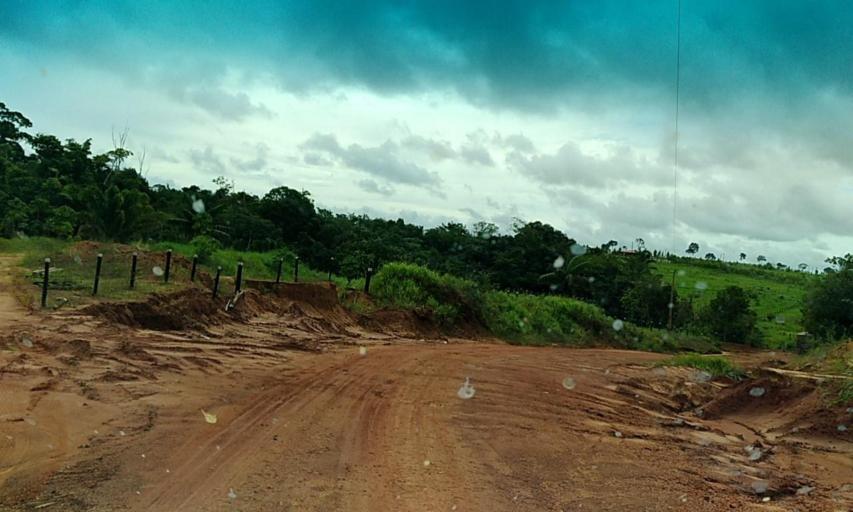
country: BR
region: Para
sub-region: Altamira
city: Altamira
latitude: -3.0626
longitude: -51.7174
